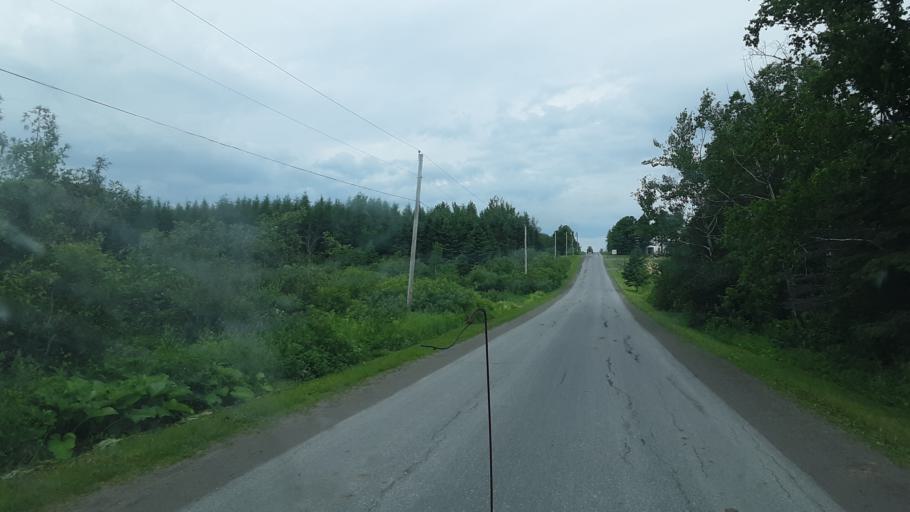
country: US
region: Maine
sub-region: Aroostook County
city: Easton
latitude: 46.6857
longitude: -67.8467
